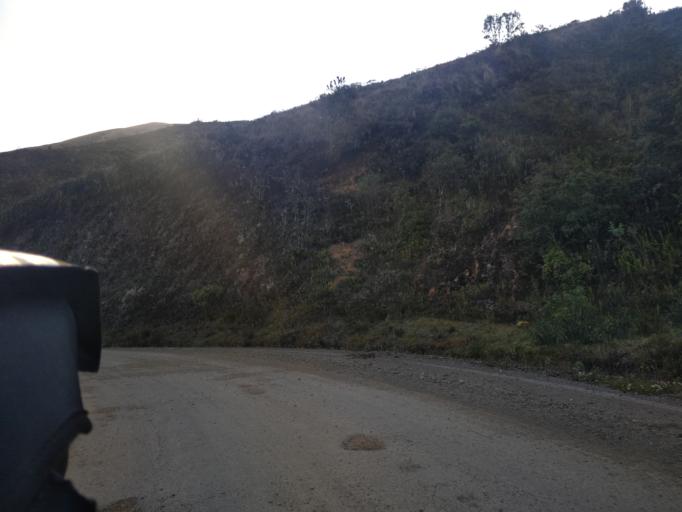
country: PE
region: Amazonas
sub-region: Provincia de Chachapoyas
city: Montevideo
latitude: -6.7152
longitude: -77.8730
